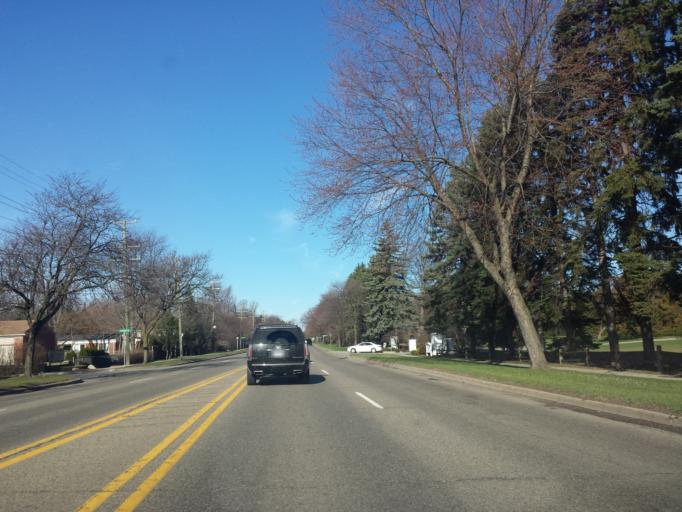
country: US
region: Michigan
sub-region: Oakland County
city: Franklin
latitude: 42.5447
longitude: -83.2893
